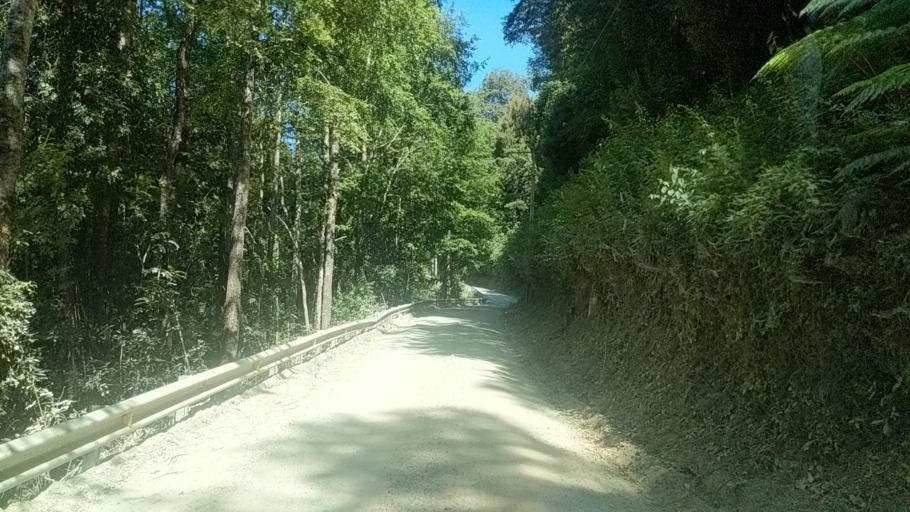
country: CL
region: Araucania
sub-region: Provincia de Cautin
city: Pucon
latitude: -39.0635
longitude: -71.7240
